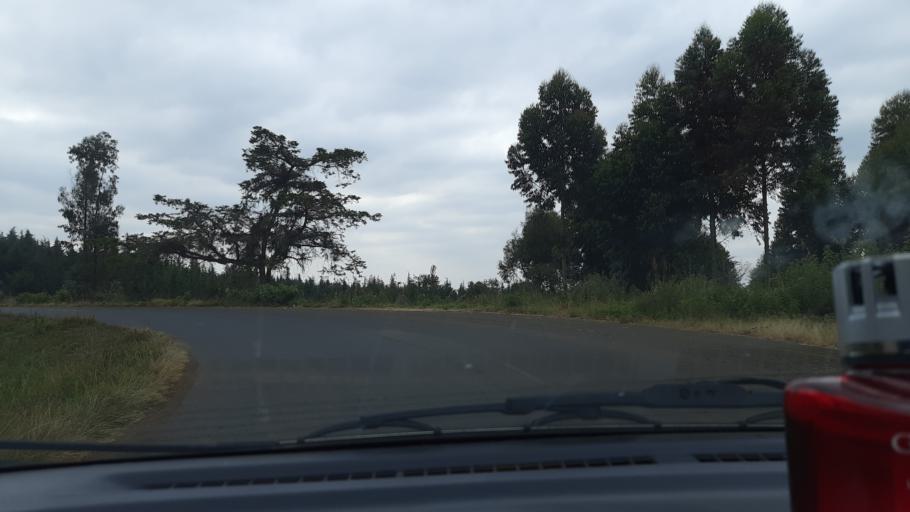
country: TZ
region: Kilimanjaro
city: Moshi
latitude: -2.9604
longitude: 37.5037
